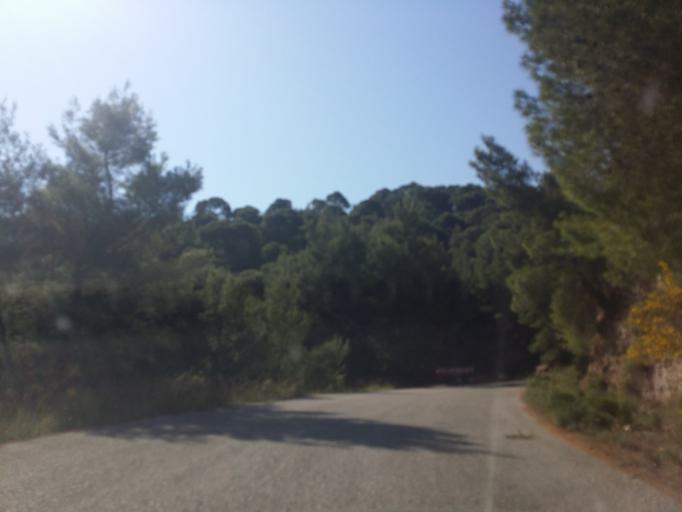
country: GR
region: Attica
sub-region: Nomos Piraios
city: Poros
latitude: 37.5217
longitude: 23.4774
